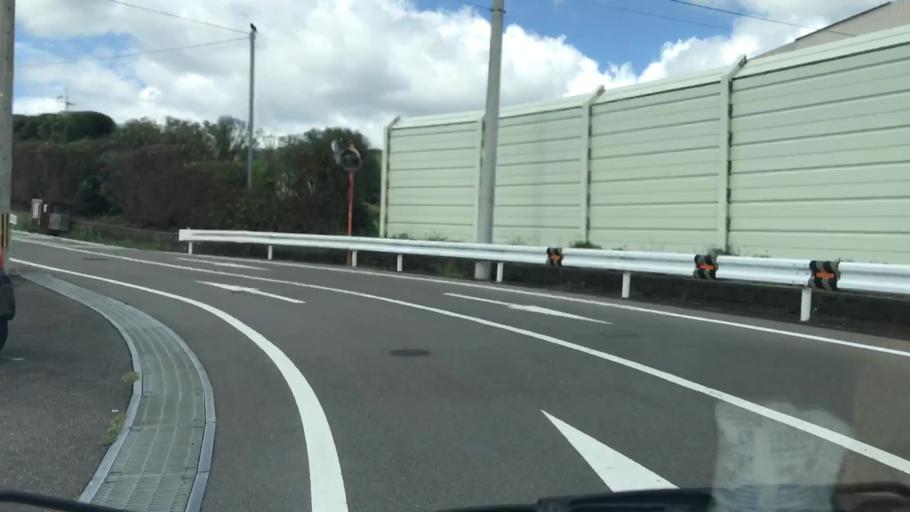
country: JP
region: Saga Prefecture
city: Takeocho-takeo
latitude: 33.2308
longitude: 130.1403
